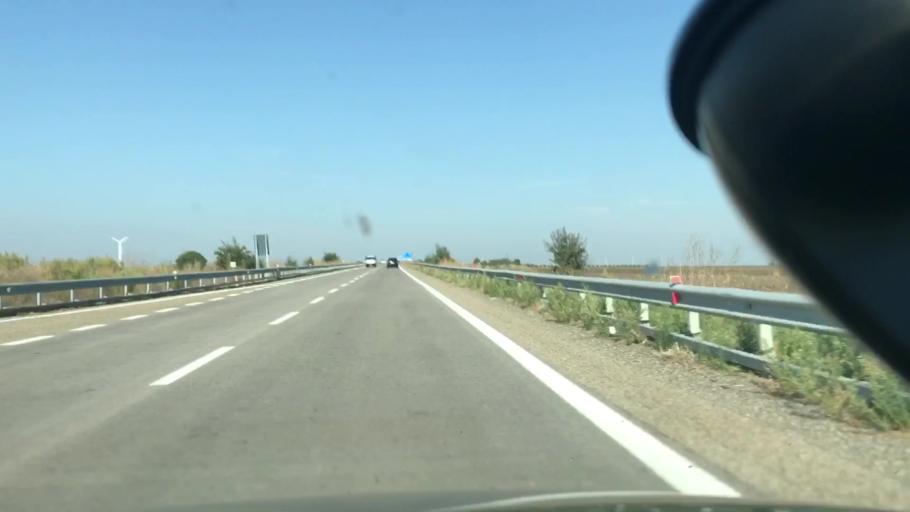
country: IT
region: Basilicate
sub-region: Provincia di Potenza
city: Montemilone
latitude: 40.9903
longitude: 15.9000
